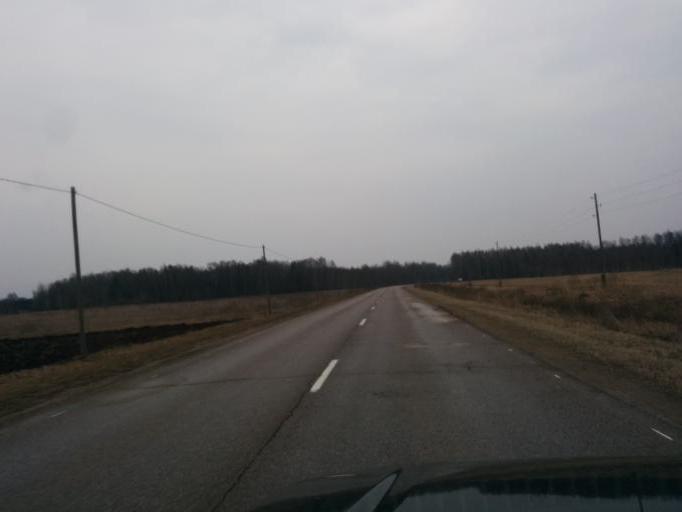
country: LV
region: Ikskile
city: Ikskile
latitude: 56.8185
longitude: 24.4595
